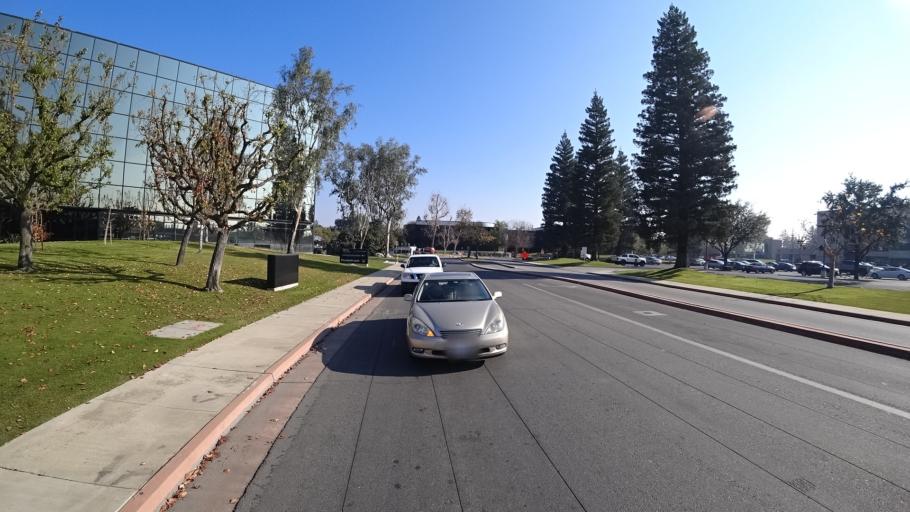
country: US
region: California
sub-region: Kern County
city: Bakersfield
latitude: 35.3588
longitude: -119.0608
